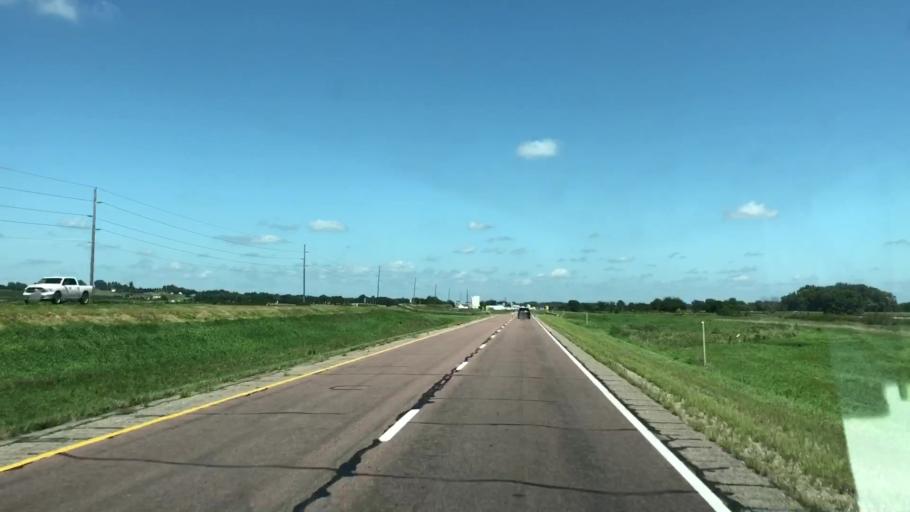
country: US
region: Iowa
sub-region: Plymouth County
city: Le Mars
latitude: 42.7017
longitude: -96.2569
